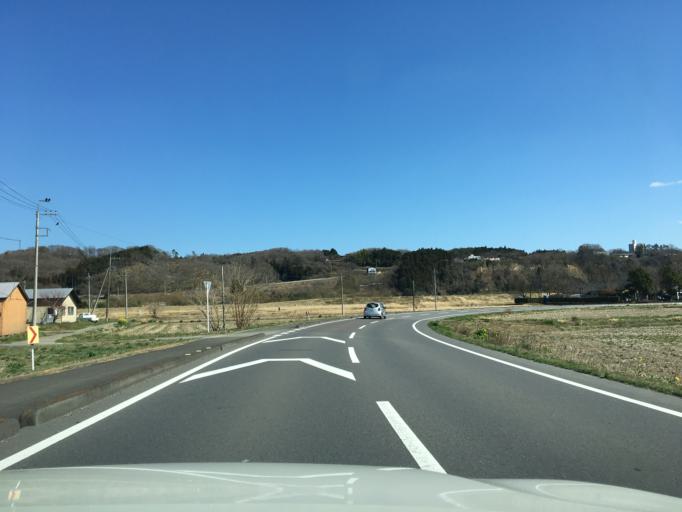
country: JP
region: Tochigi
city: Karasuyama
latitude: 36.7682
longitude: 140.1332
